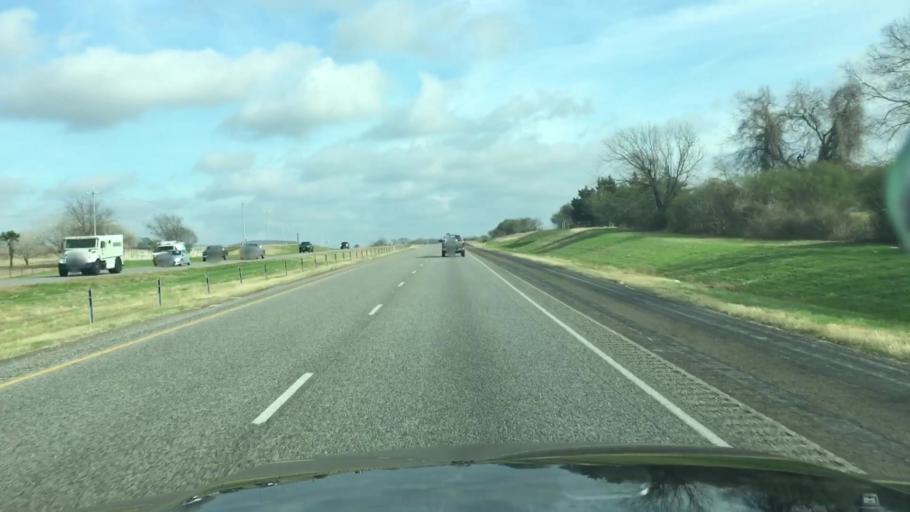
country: US
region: Texas
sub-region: Washington County
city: Brenham
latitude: 30.1365
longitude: -96.3408
